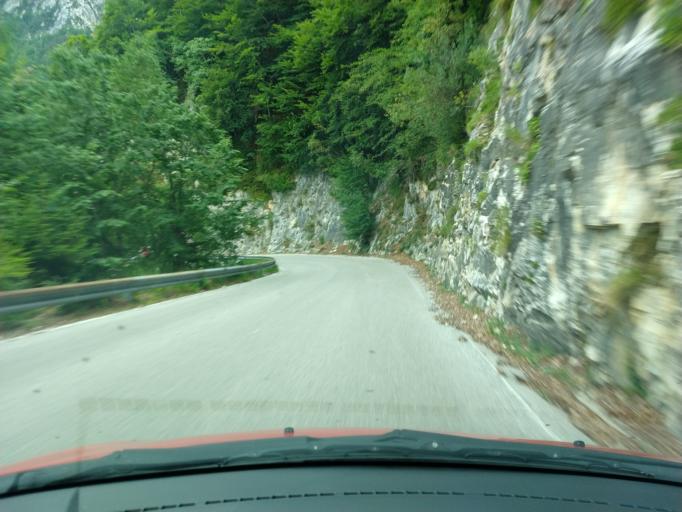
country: IT
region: Veneto
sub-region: Provincia di Vicenza
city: Tonezza del Cimone
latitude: 45.8783
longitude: 11.3229
